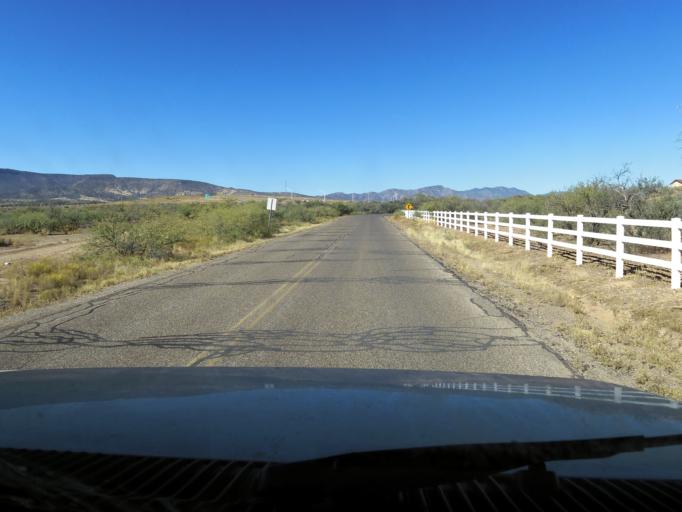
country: US
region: Arizona
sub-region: Yavapai County
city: Camp Verde
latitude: 34.5985
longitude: -111.8924
